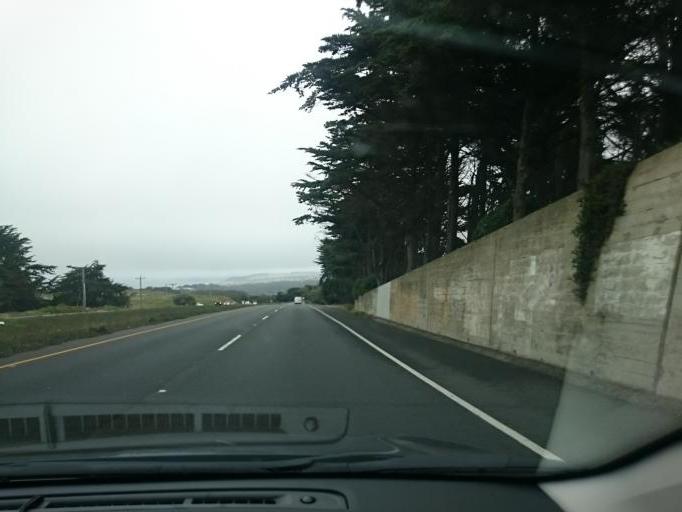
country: US
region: California
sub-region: San Mateo County
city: Broadmoor
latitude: 37.7118
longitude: -122.4980
